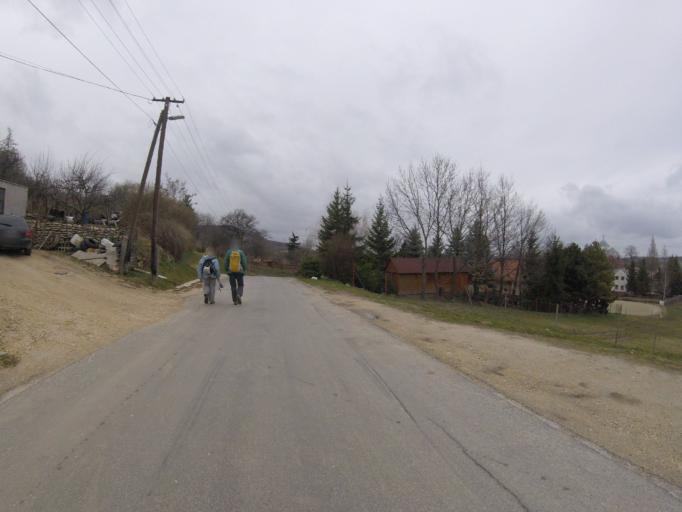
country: HU
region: Gyor-Moson-Sopron
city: Bakonyszentlaszlo
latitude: 47.3520
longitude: 17.8833
